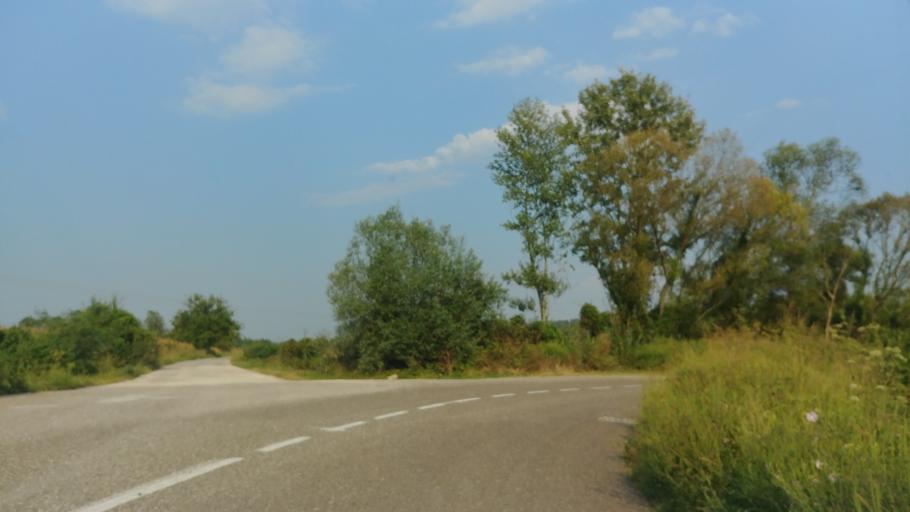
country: BA
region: Republika Srpska
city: Lopare
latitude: 44.7426
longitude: 18.8757
